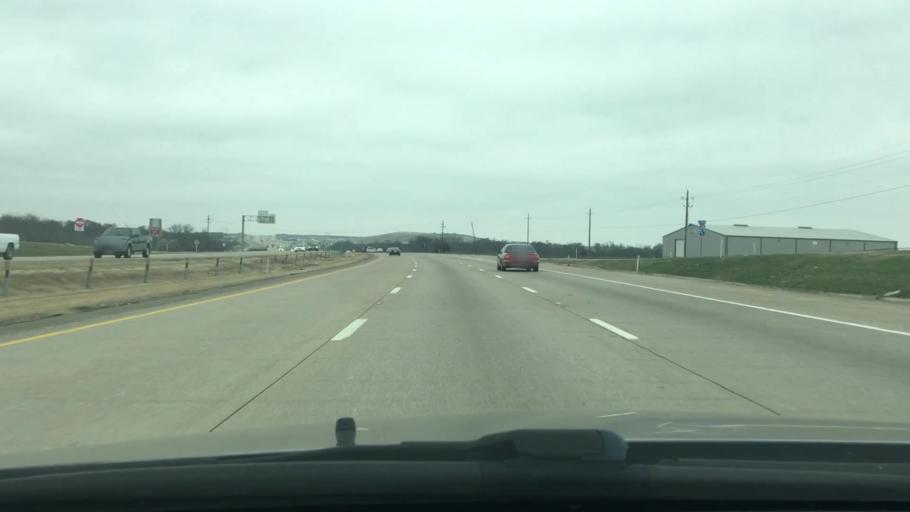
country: US
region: Texas
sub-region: Ellis County
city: Palmer
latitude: 32.4146
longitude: -96.6599
